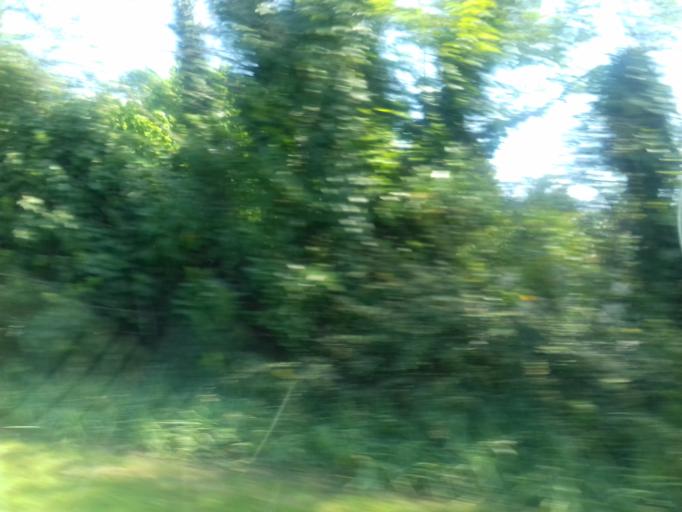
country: IE
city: Darndale
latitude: 53.3943
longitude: -6.1896
